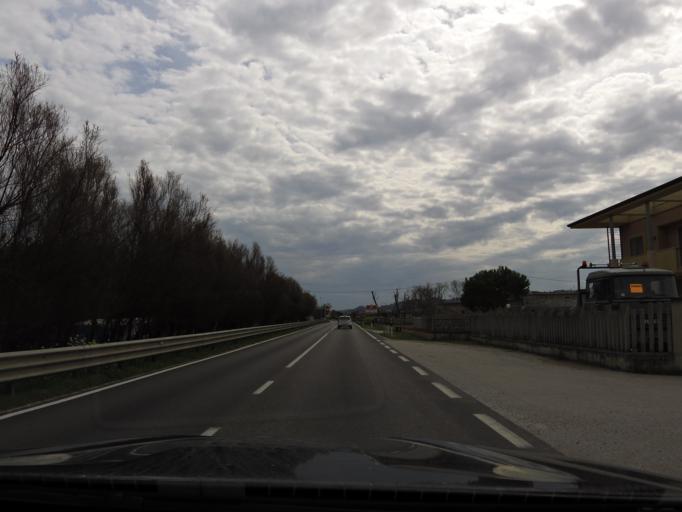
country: IT
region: The Marches
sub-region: Provincia di Macerata
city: Porto Recanati
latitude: 43.4035
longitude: 13.6778
